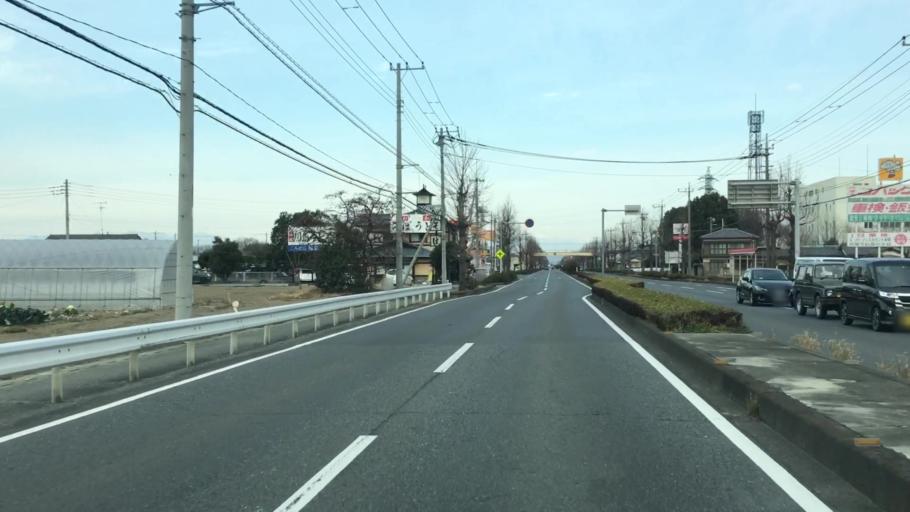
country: JP
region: Saitama
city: Menuma
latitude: 36.1863
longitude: 139.3701
